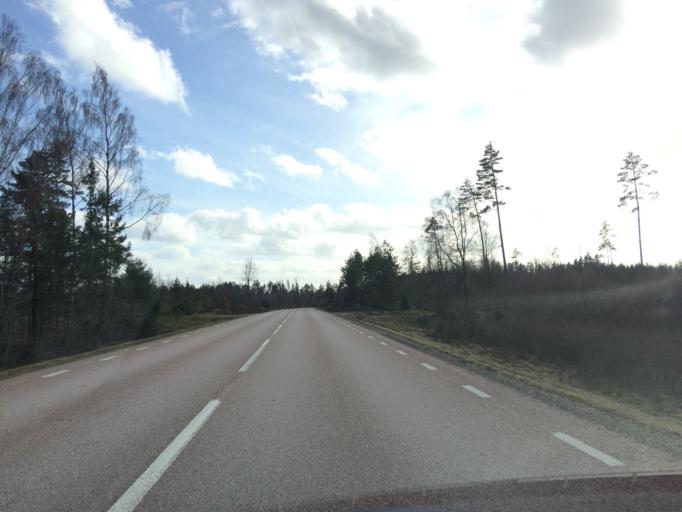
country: SE
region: Kronoberg
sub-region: Markaryds Kommun
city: Stromsnasbruk
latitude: 56.7987
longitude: 13.5611
